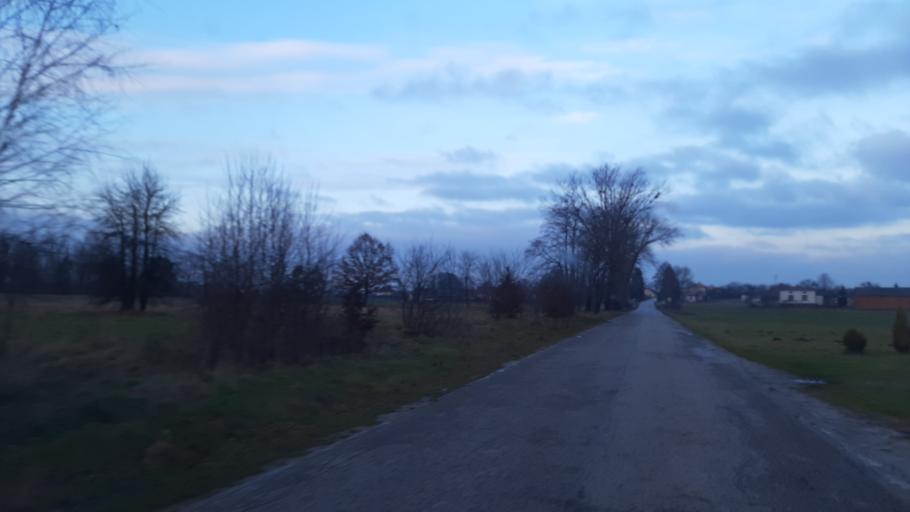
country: PL
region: Lublin Voivodeship
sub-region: Powiat lubartowski
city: Kamionka
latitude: 51.3985
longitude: 22.4111
